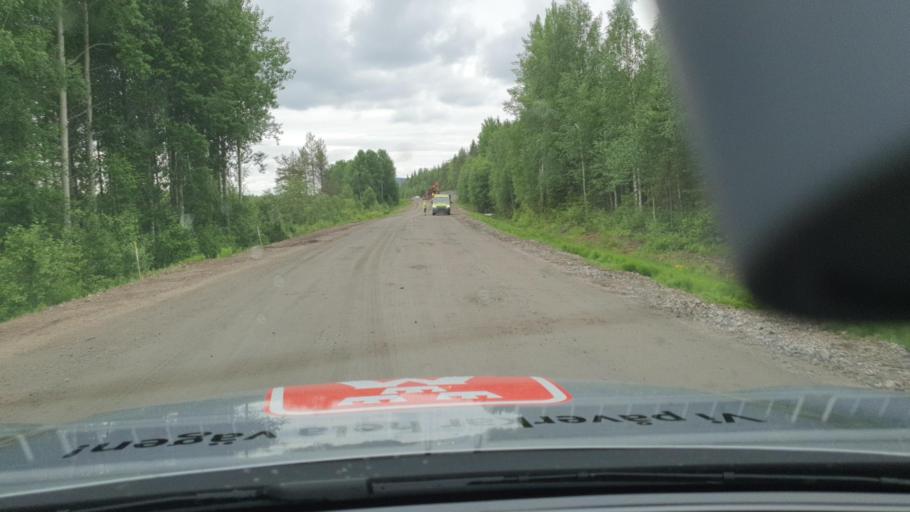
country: SE
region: Norrbotten
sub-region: Overtornea Kommun
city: OEvertornea
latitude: 66.4108
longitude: 23.6025
